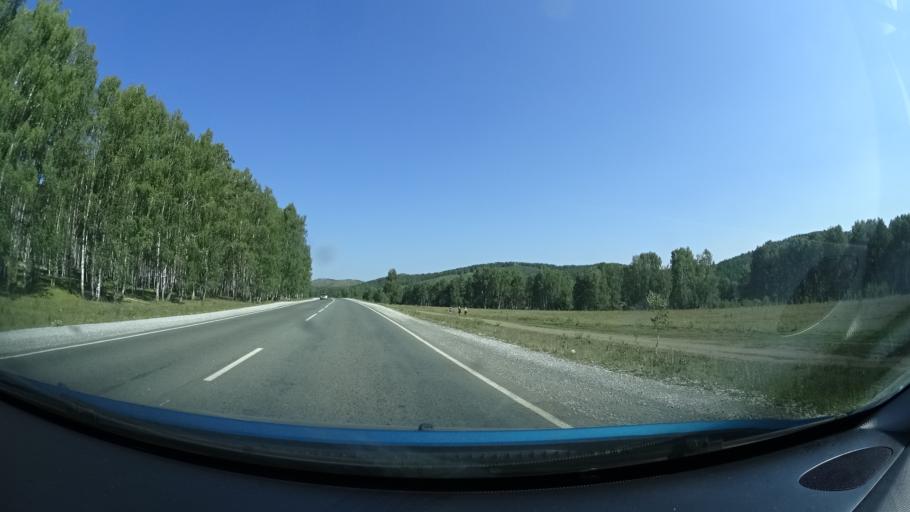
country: RU
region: Bashkortostan
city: Abzakovo
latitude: 53.8436
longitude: 58.5823
